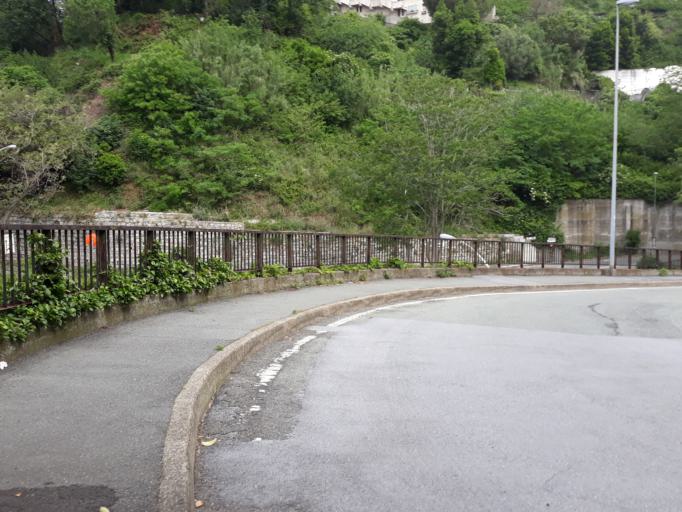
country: IT
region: Liguria
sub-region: Provincia di Genova
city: Mele
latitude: 44.4318
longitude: 8.7700
